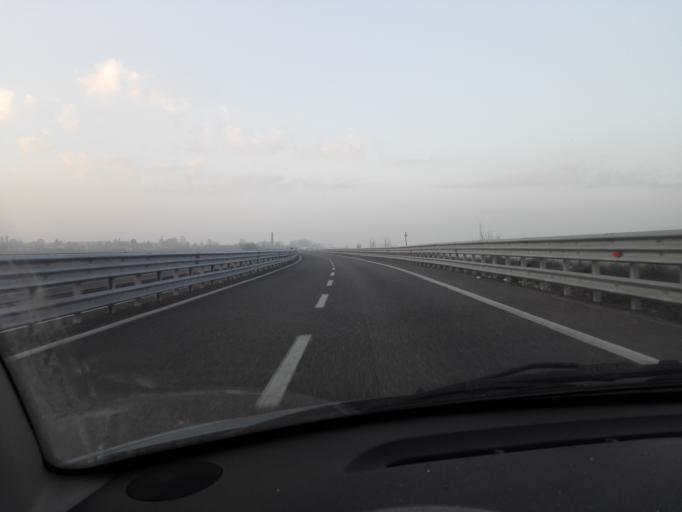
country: IT
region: Piedmont
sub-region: Provincia di Alessandria
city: Alessandria
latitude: 44.9140
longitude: 8.6413
